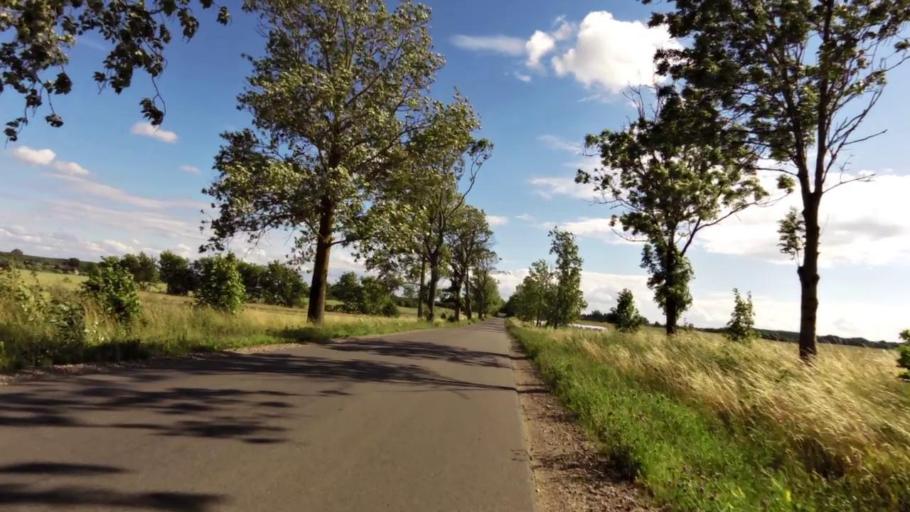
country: PL
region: West Pomeranian Voivodeship
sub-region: Powiat slawienski
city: Slawno
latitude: 54.4419
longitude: 16.7343
